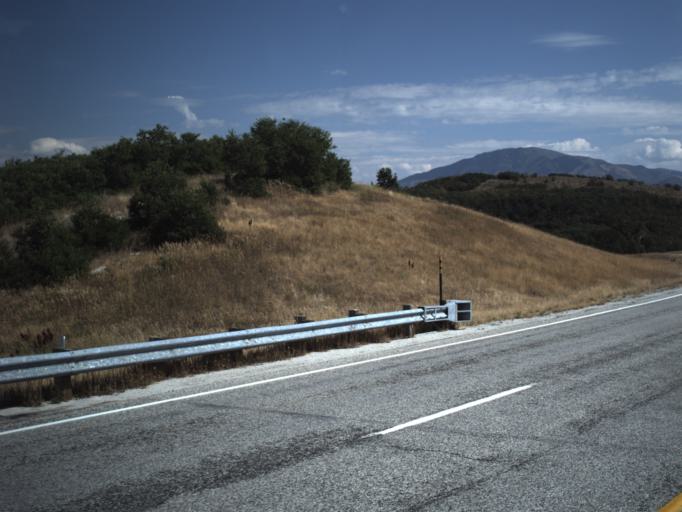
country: US
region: Utah
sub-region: Morgan County
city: Mountain Green
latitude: 41.1867
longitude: -111.8110
